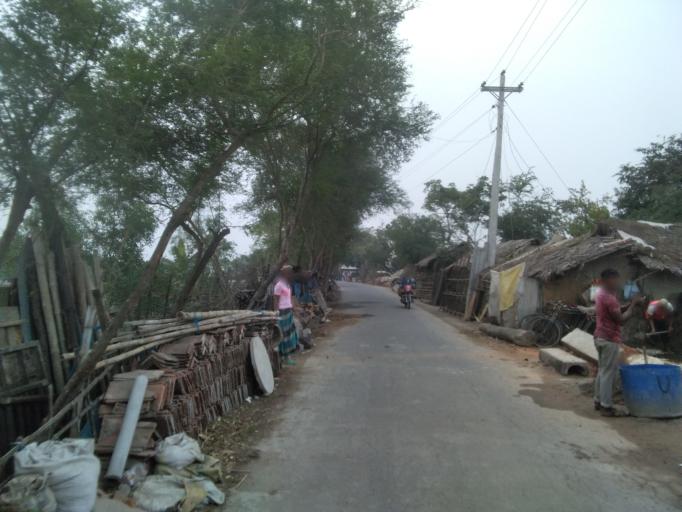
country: BD
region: Khulna
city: Satkhira
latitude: 22.5830
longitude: 89.0670
